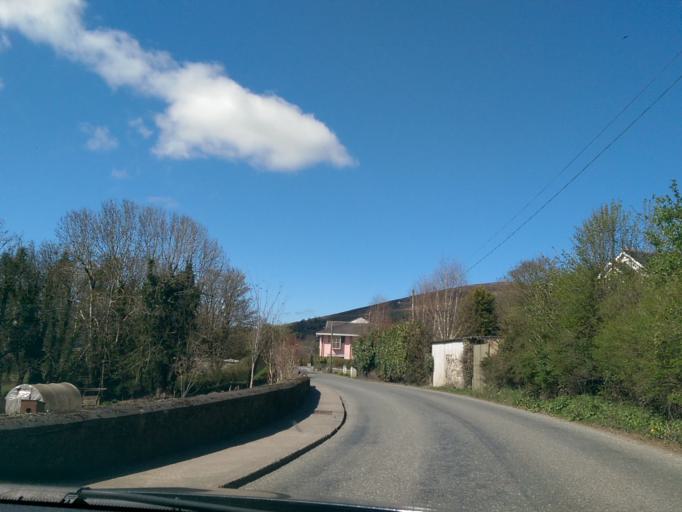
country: IE
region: Leinster
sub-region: Wicklow
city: Carnew
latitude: 52.7994
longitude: -6.4609
